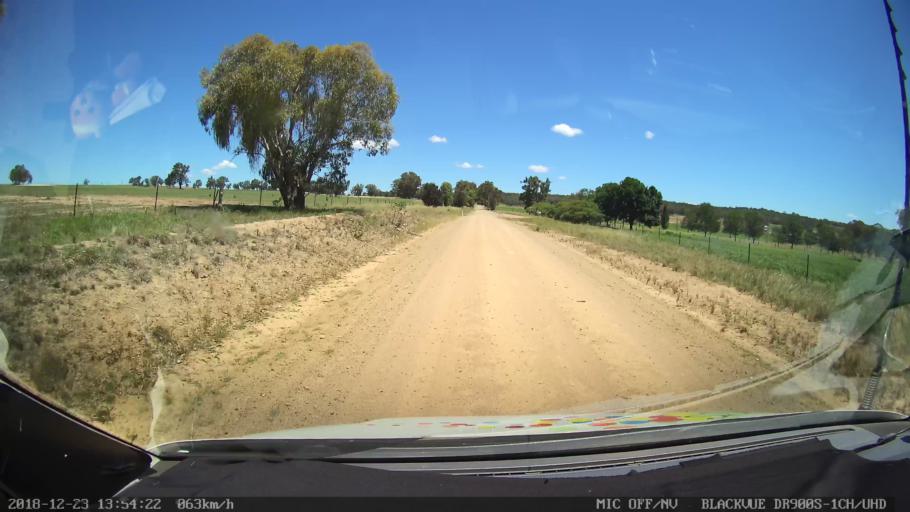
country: AU
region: New South Wales
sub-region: Tamworth Municipality
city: Manilla
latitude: -30.5603
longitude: 151.0908
